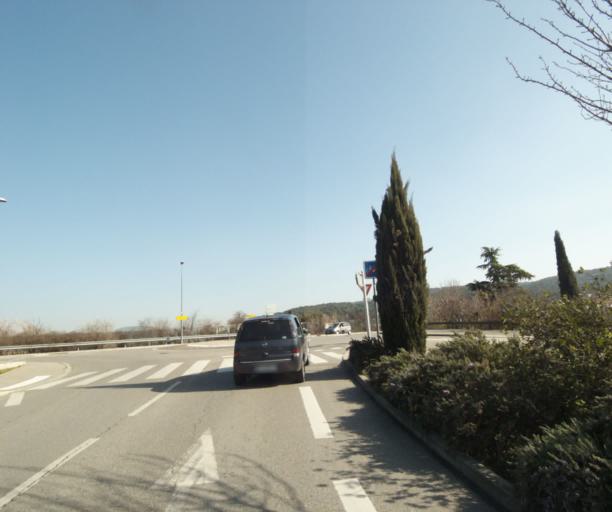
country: FR
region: Provence-Alpes-Cote d'Azur
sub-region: Departement des Bouches-du-Rhone
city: Aix-en-Provence
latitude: 43.5121
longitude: 5.4633
